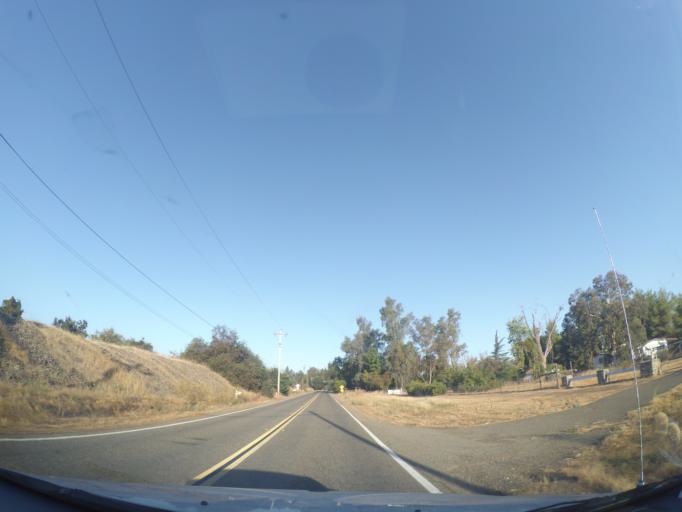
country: US
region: California
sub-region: Merced County
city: Merced
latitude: 37.5216
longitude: -120.4040
